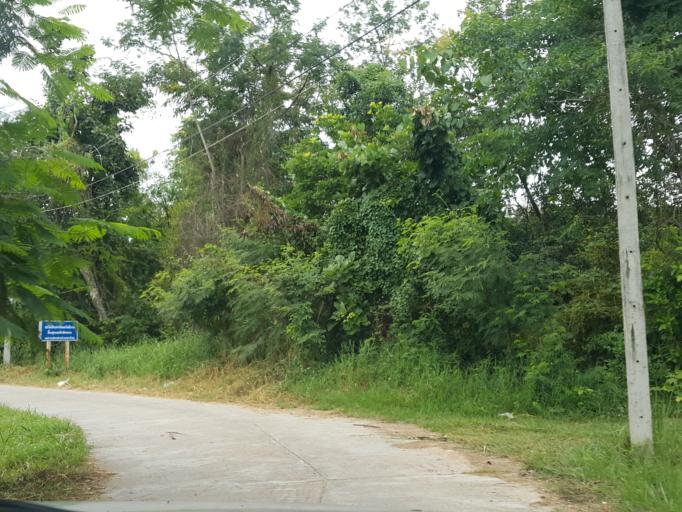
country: TH
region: Chiang Mai
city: San Sai
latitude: 18.8216
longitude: 99.1124
